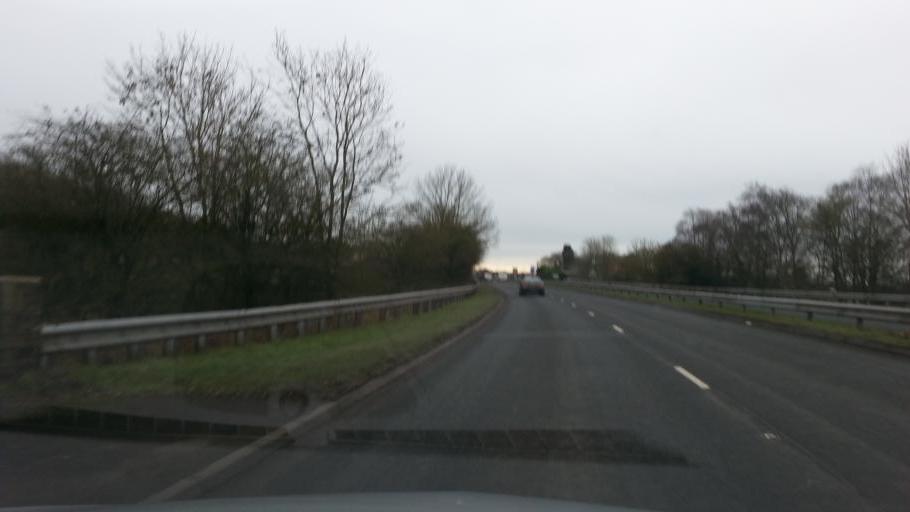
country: GB
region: England
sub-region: Solihull
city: Tidbury Green
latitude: 52.3609
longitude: -1.8894
